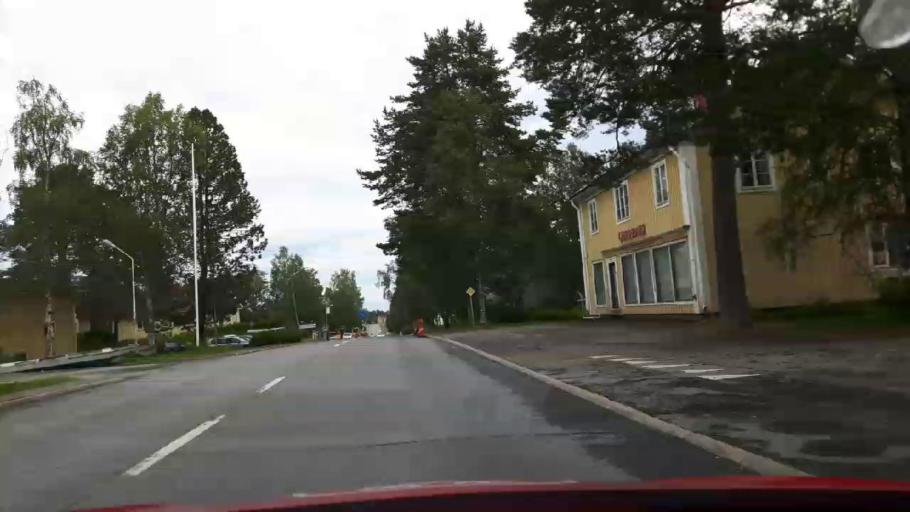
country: SE
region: Jaemtland
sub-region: Stroemsunds Kommun
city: Stroemsund
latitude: 63.5844
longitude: 15.3521
